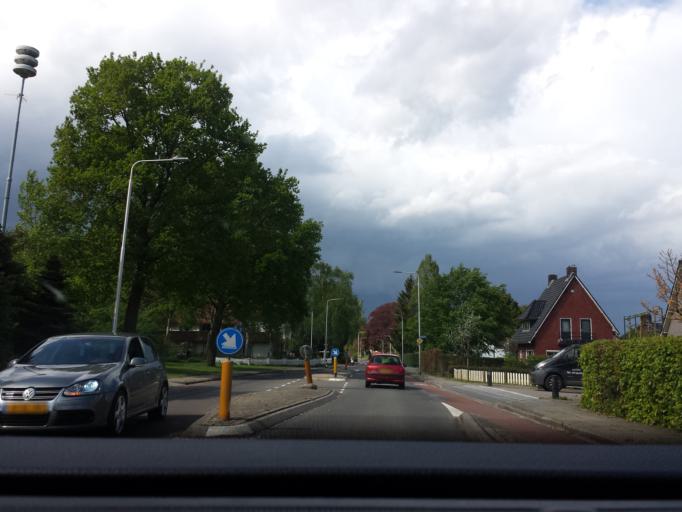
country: NL
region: Gelderland
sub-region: Gemeente Lochem
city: Lochem
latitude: 52.1519
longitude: 6.4191
